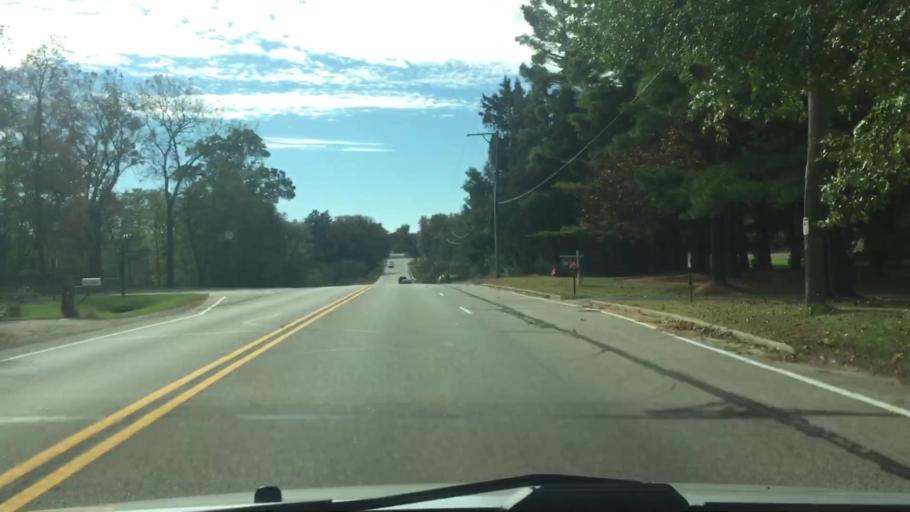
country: US
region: Wisconsin
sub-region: Waukesha County
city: Dousman
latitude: 42.9927
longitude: -88.4635
